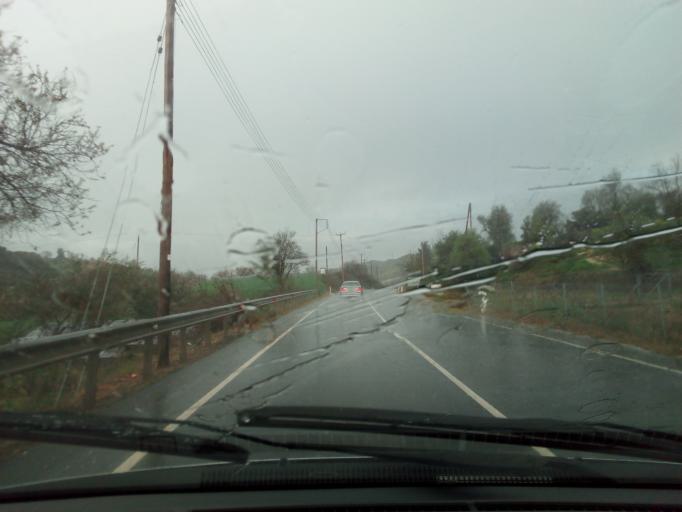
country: CY
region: Pafos
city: Polis
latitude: 34.9471
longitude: 32.4680
